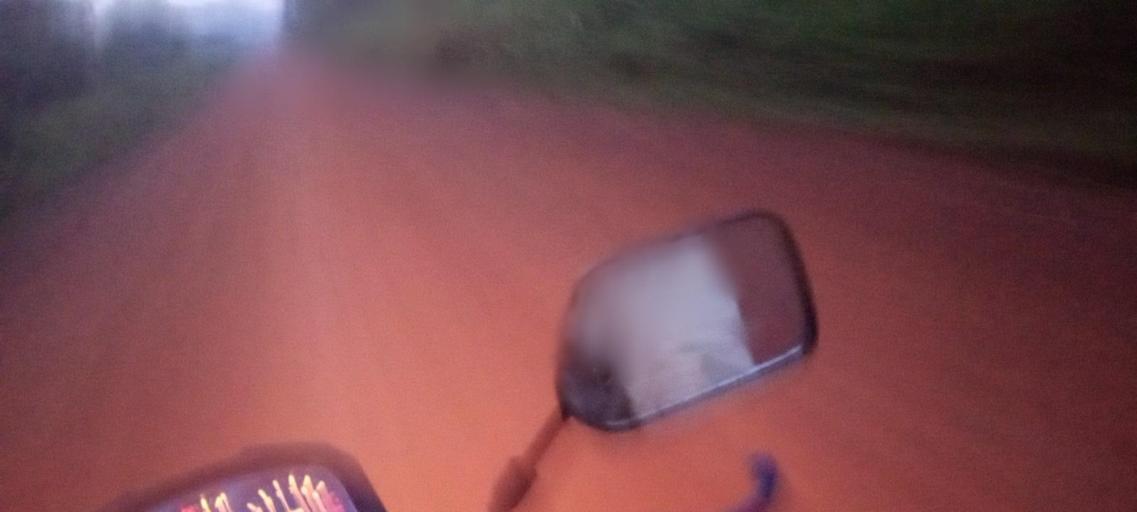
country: CD
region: Eastern Province
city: Kisangani
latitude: -0.1508
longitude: 25.6352
